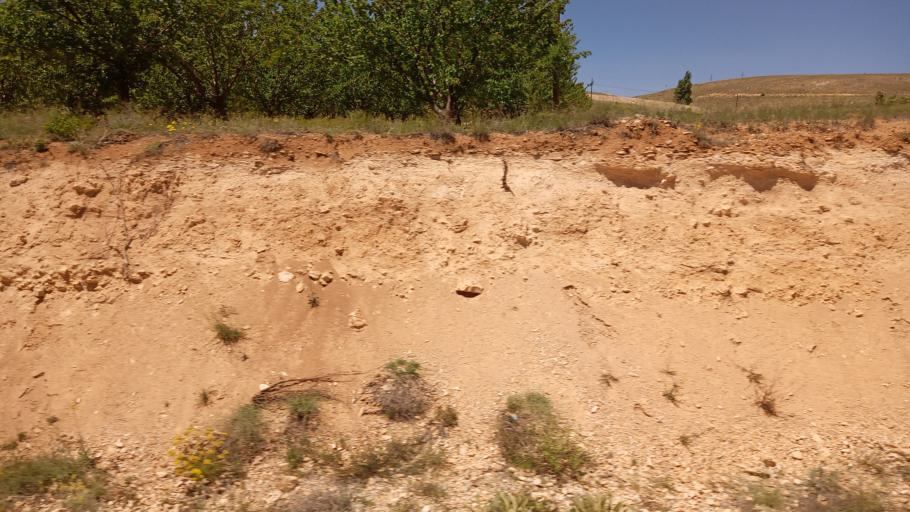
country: TR
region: Malatya
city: Darende
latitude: 38.5997
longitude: 37.4628
